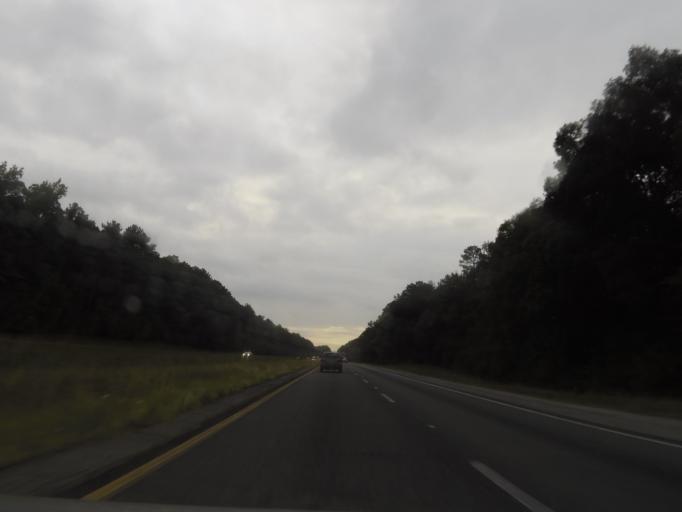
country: US
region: Alabama
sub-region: Saint Clair County
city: Springville
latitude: 33.7525
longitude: -86.4817
